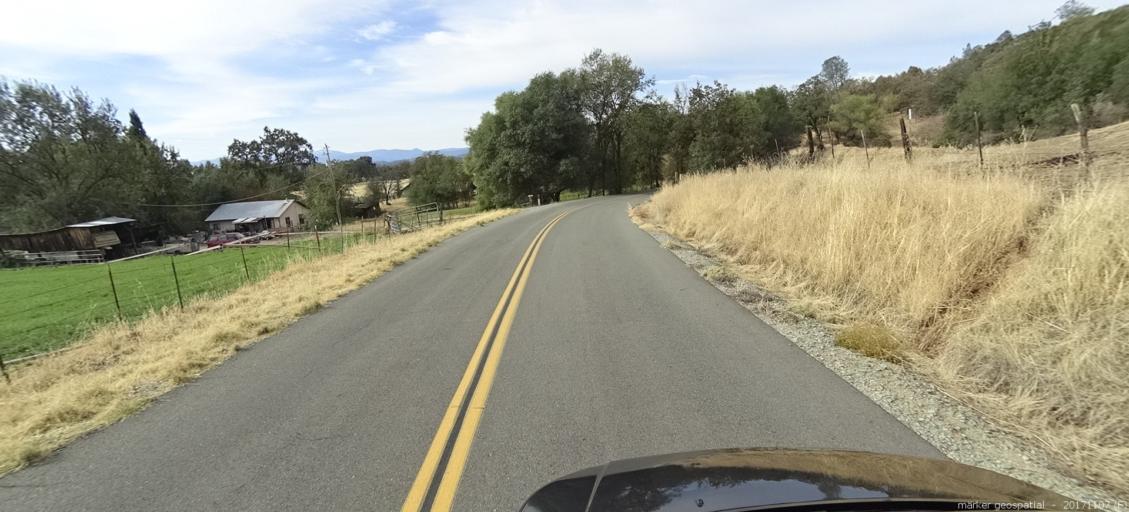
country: US
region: California
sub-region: Shasta County
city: Shasta
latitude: 40.5023
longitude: -122.5557
